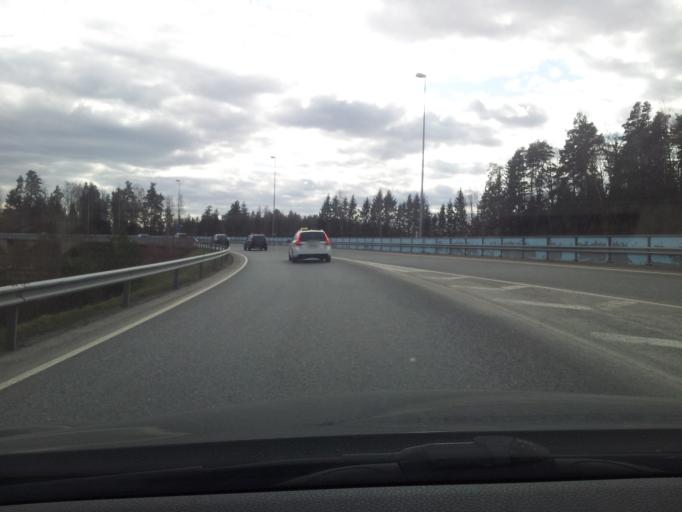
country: FI
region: Uusimaa
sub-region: Helsinki
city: Kauniainen
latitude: 60.2052
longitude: 24.7435
